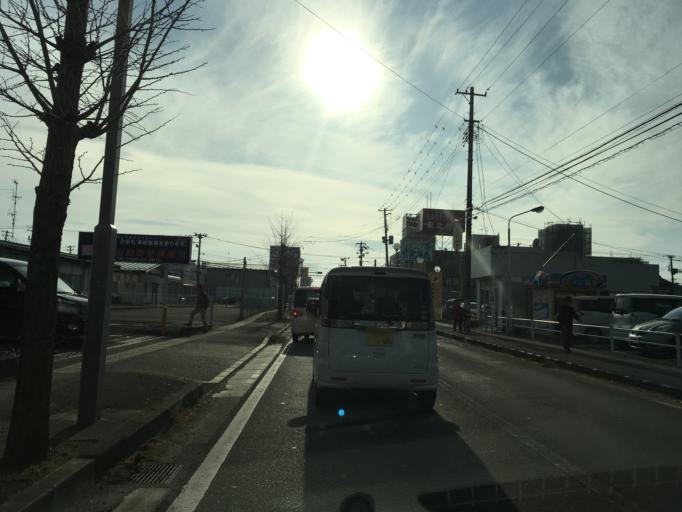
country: JP
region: Miyagi
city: Wakuya
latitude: 38.6906
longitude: 141.1902
